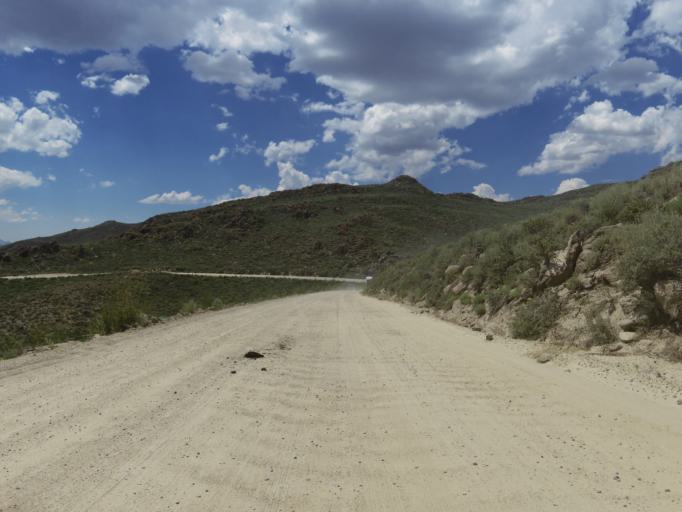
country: US
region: California
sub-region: Mono County
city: Bridgeport
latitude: 38.1979
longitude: -119.0353
